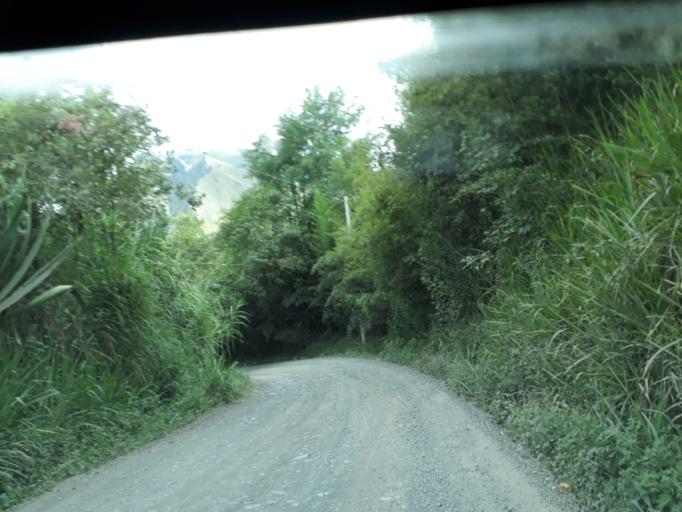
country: CO
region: Cundinamarca
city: Pacho
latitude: 5.1887
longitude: -74.1940
